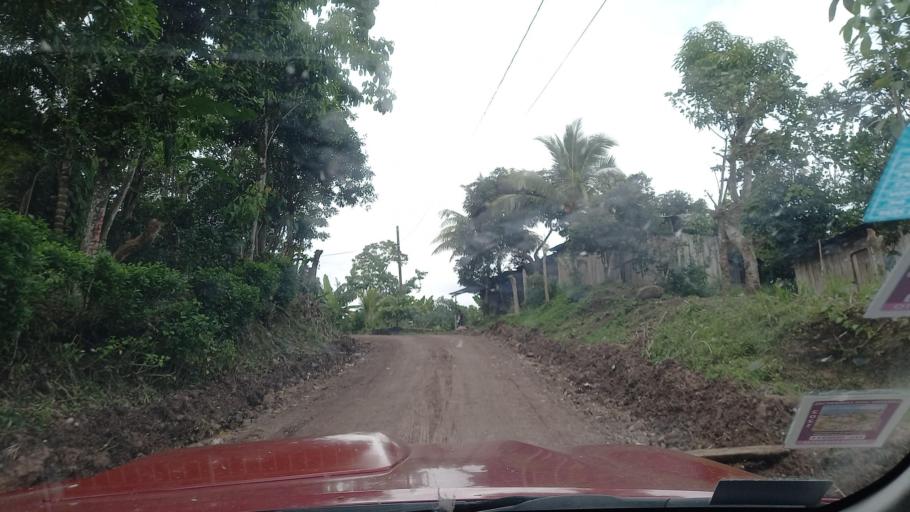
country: NI
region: Jinotega
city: San Jose de Bocay
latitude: 13.3484
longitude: -85.6591
